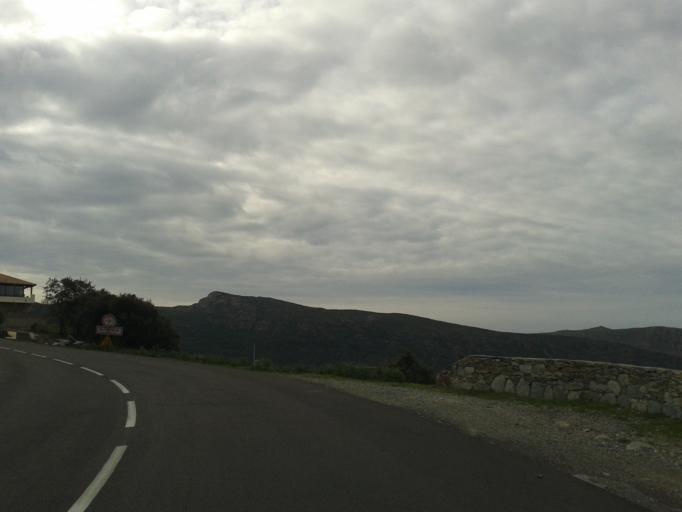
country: FR
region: Corsica
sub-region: Departement de la Haute-Corse
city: Brando
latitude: 42.9767
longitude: 9.3842
